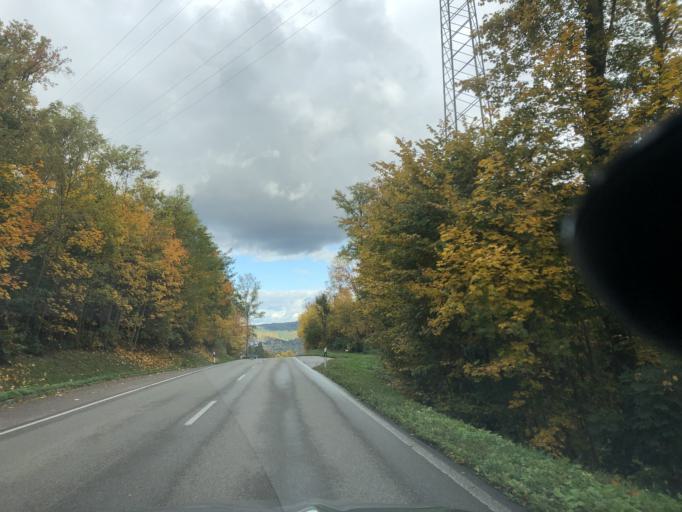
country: DE
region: Baden-Wuerttemberg
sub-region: Regierungsbezirk Stuttgart
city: Winterbach
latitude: 48.7846
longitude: 9.4610
